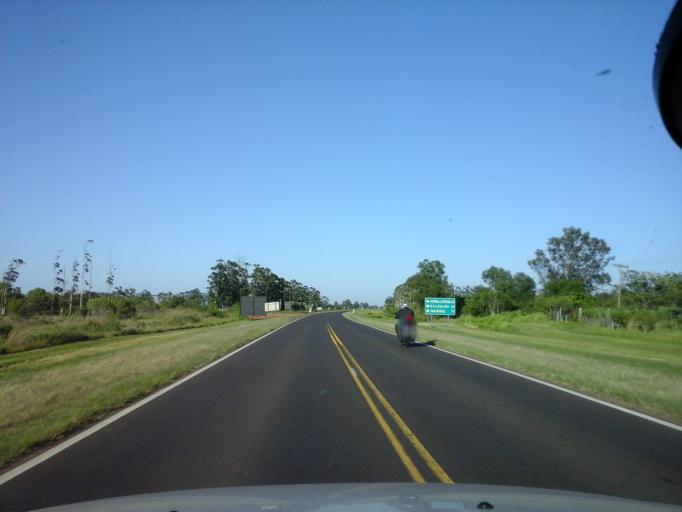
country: AR
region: Corrientes
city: Ita Ibate
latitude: -27.4404
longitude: -57.3535
